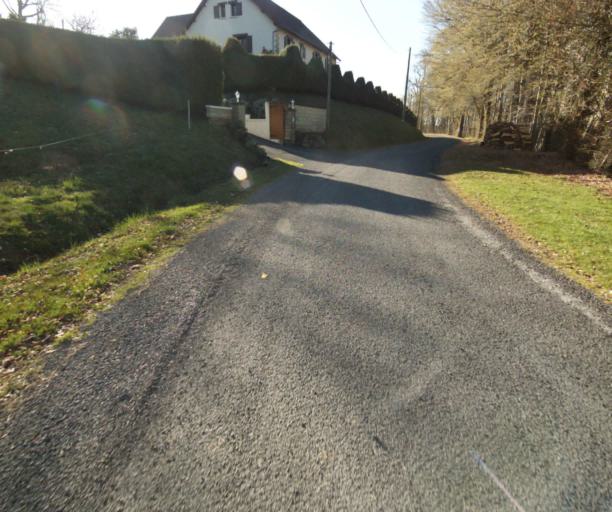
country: FR
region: Limousin
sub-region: Departement de la Correze
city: Seilhac
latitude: 45.3665
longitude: 1.7539
